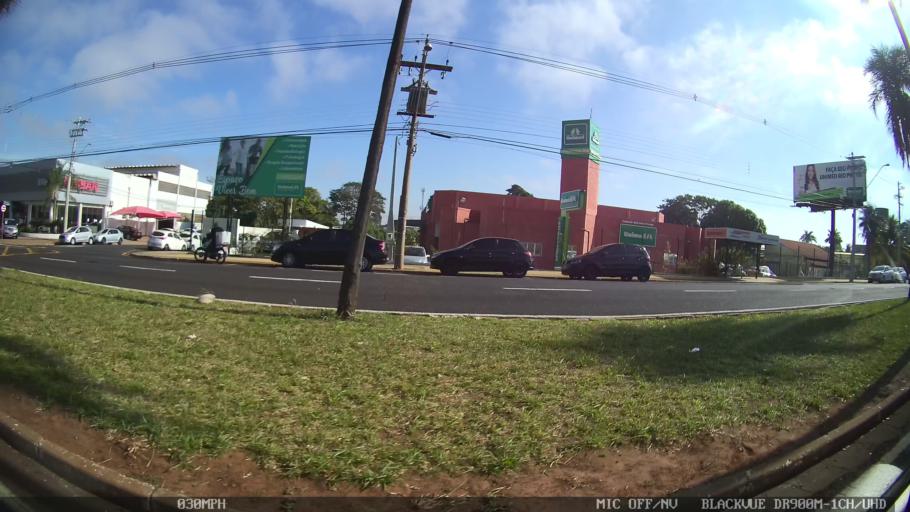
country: BR
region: Sao Paulo
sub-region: Sao Jose Do Rio Preto
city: Sao Jose do Rio Preto
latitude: -20.8211
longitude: -49.4162
